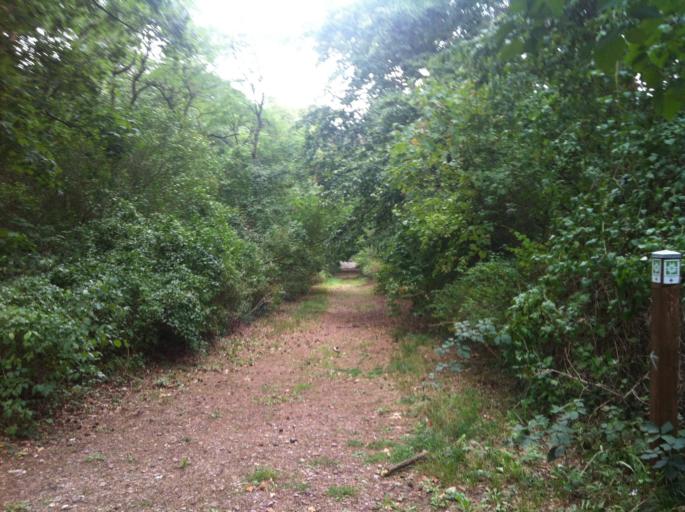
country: DE
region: Rheinland-Pfalz
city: Budenheim
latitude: 50.0098
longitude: 8.1796
